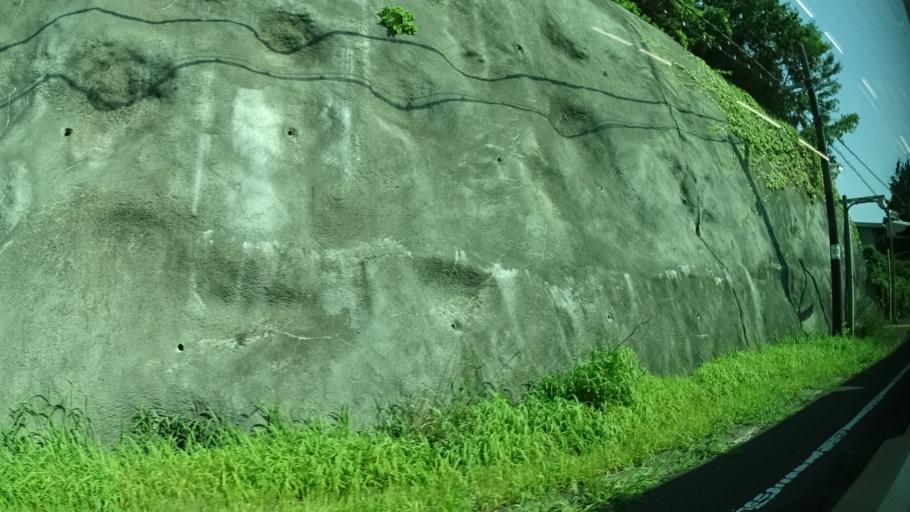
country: JP
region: Miyagi
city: Matsushima
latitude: 38.3807
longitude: 141.0667
